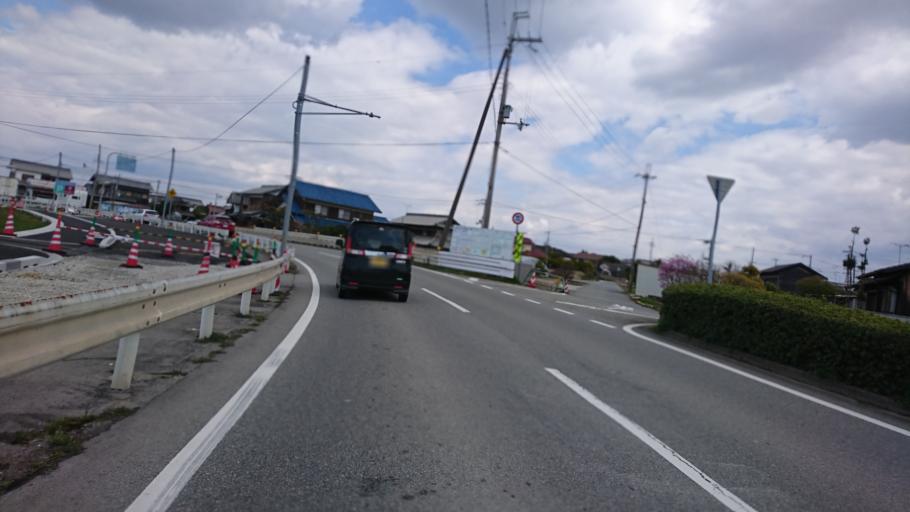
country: JP
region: Hyogo
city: Miki
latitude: 34.7589
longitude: 134.9501
